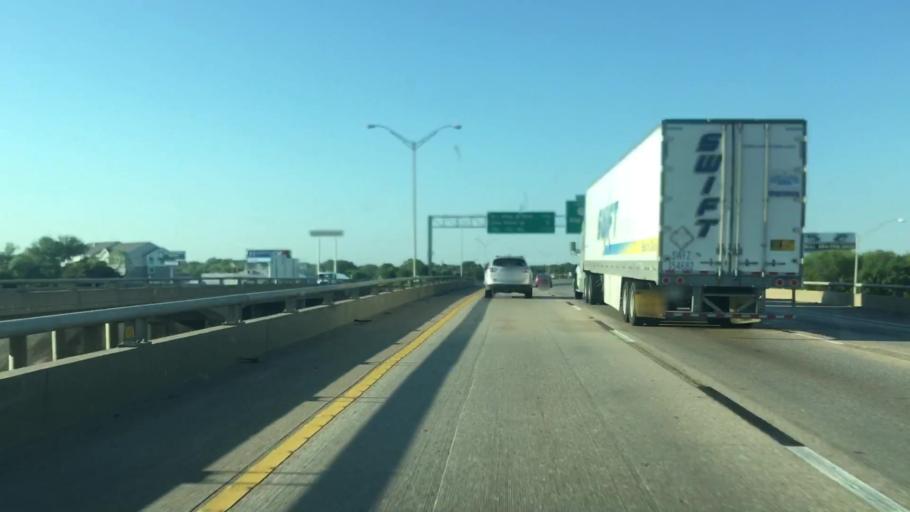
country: US
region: Texas
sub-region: McLennan County
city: Bellmead
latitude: 31.5848
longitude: -97.1099
